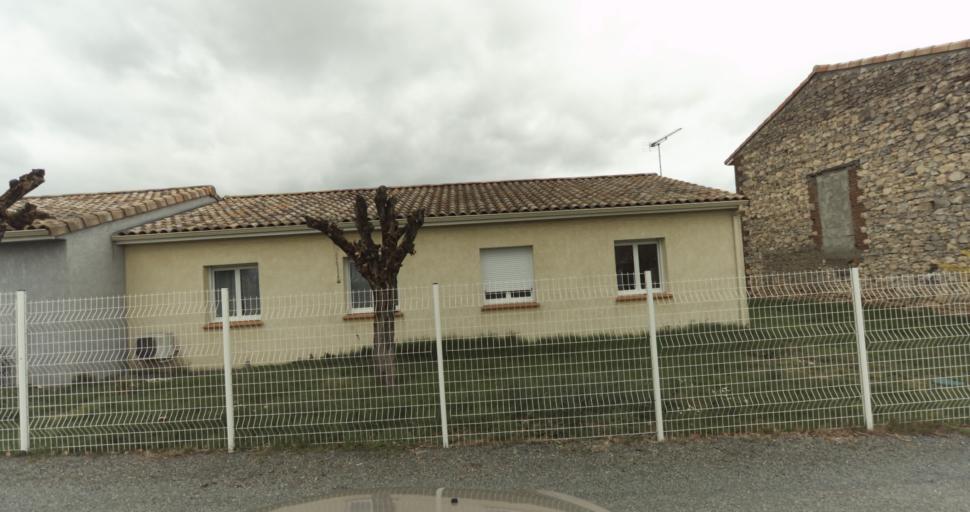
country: FR
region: Midi-Pyrenees
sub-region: Departement du Tarn
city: Puygouzon
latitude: 43.9001
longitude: 2.1672
